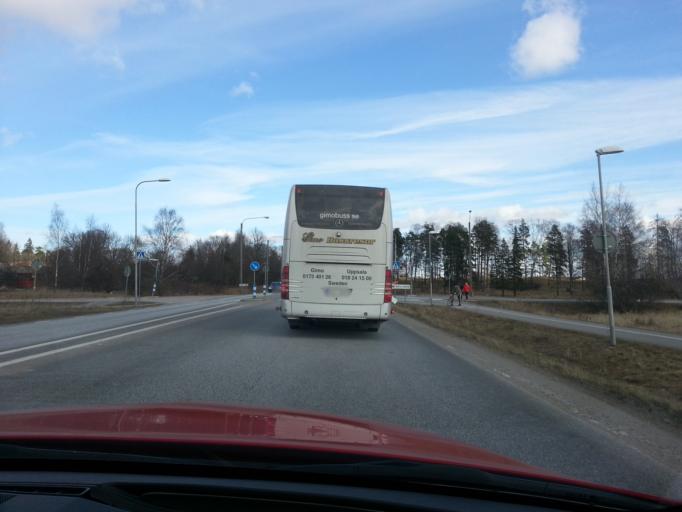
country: SE
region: Uppsala
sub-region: Uppsala Kommun
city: Uppsala
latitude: 59.8770
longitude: 17.6791
